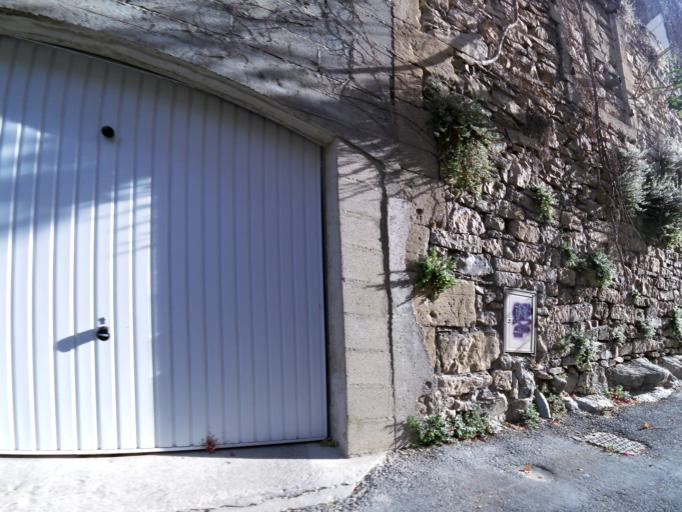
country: FR
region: Languedoc-Roussillon
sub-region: Departement du Gard
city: Calvisson
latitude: 43.7856
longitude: 4.1892
